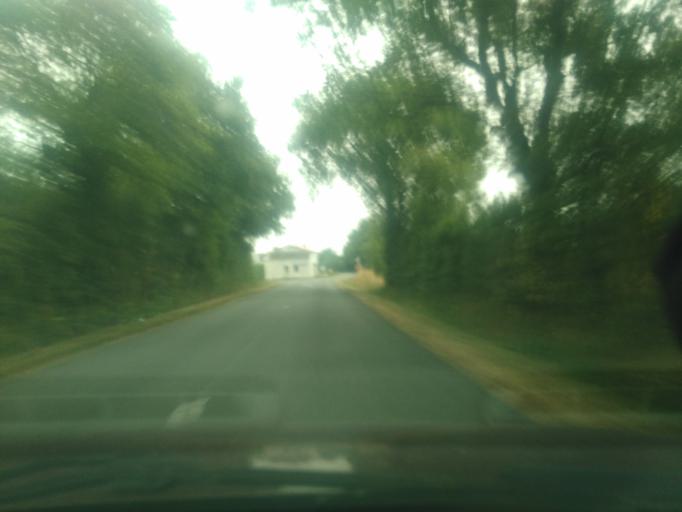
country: FR
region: Pays de la Loire
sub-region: Departement de la Vendee
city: Chauche
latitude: 46.7856
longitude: -1.3022
